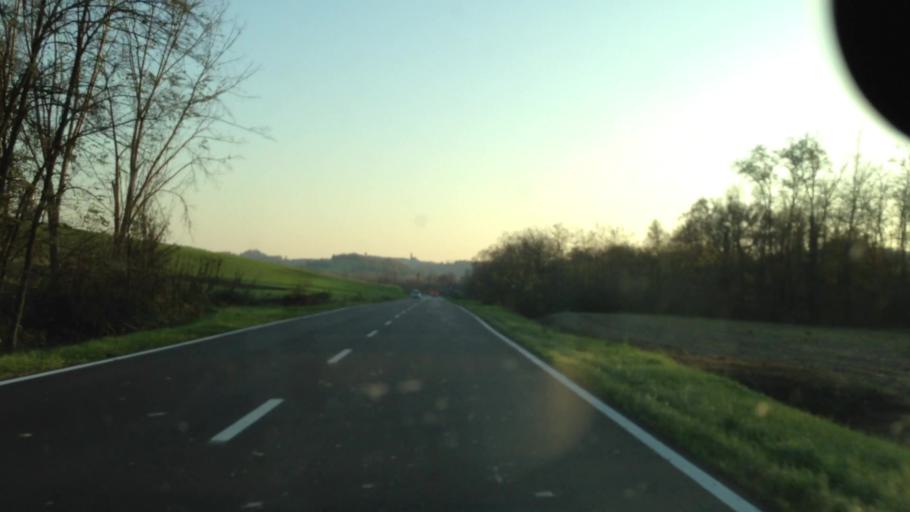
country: IT
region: Piedmont
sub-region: Provincia di Asti
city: Cunico
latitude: 45.0449
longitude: 8.1118
